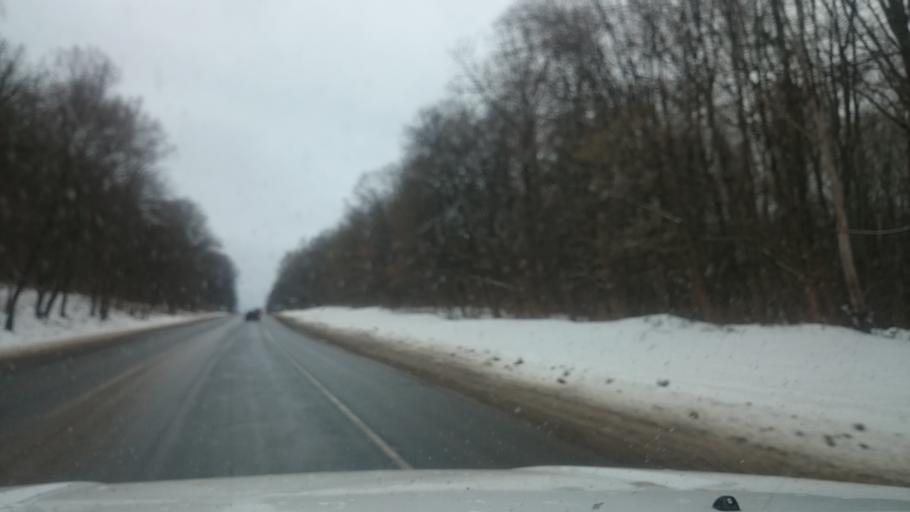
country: RU
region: Tula
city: Kosaya Gora
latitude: 54.0945
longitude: 37.5488
